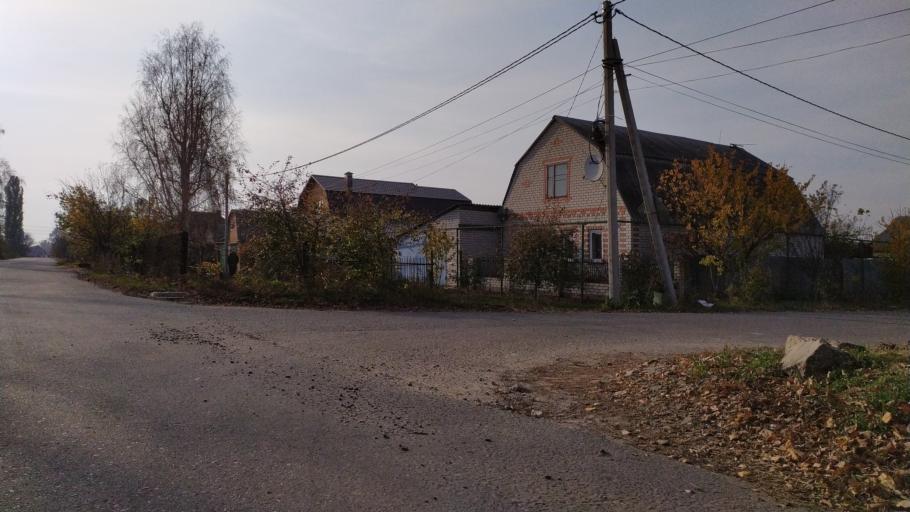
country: RU
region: Kursk
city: Kursk
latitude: 51.6426
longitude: 36.1506
